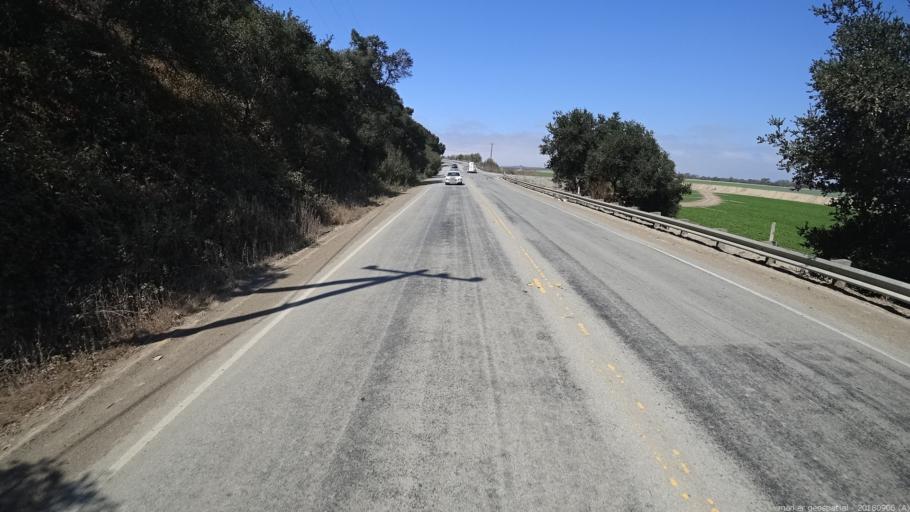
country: US
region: California
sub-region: Monterey County
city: Boronda
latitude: 36.6531
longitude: -121.7259
